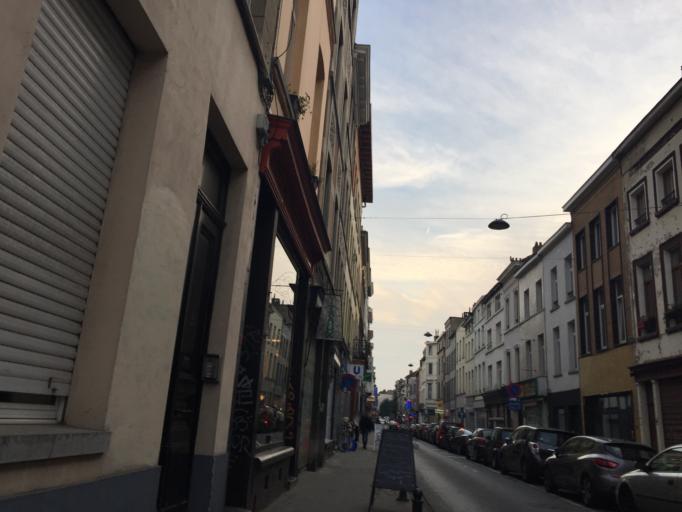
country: BE
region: Brussels Capital
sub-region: Bruxelles-Capitale
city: Brussels
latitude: 50.8376
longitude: 4.3676
